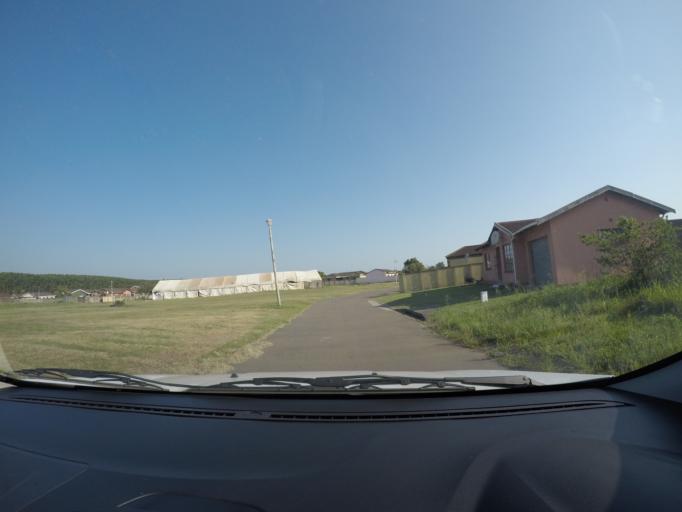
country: ZA
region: KwaZulu-Natal
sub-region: uThungulu District Municipality
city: Richards Bay
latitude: -28.7106
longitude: 32.0379
